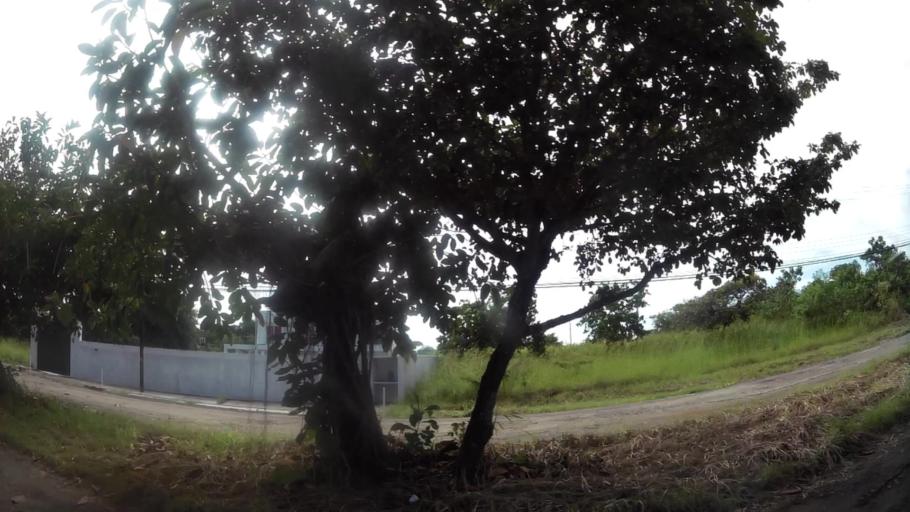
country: PA
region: Panama
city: Nueva Gorgona
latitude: 8.5457
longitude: -79.8970
